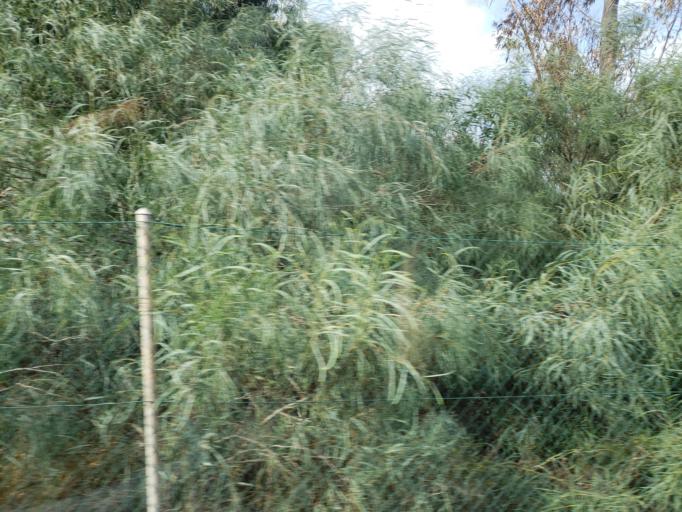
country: PT
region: Faro
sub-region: Portimao
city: Alvor
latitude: 37.1644
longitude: -8.5776
